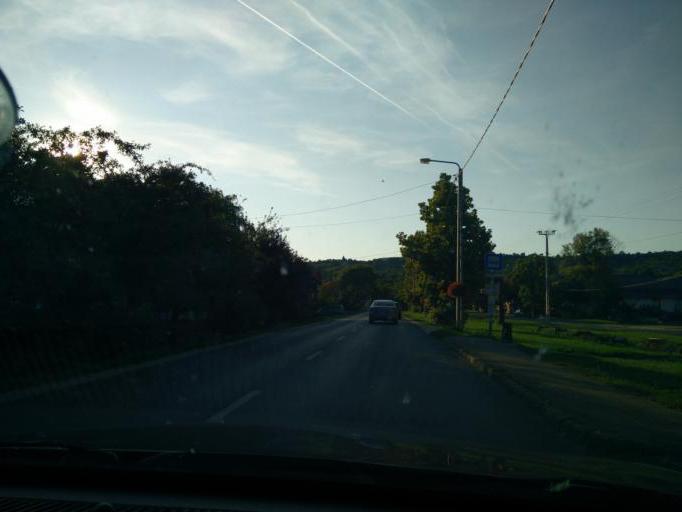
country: HU
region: Pest
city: Zsambek
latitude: 47.5460
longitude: 18.7245
